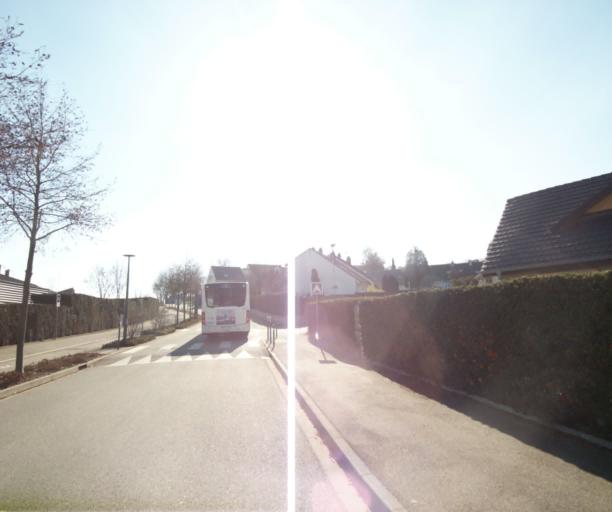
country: FR
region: Lorraine
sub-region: Departement de Meurthe-et-Moselle
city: Vandoeuvre-les-Nancy
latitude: 48.6534
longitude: 6.1760
